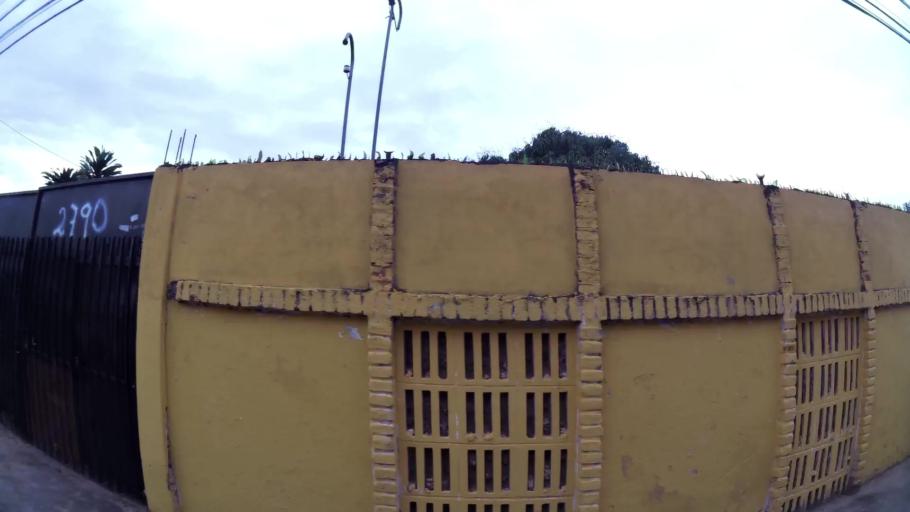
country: BO
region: Santa Cruz
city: Santa Cruz de la Sierra
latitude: -17.7737
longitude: -63.1564
